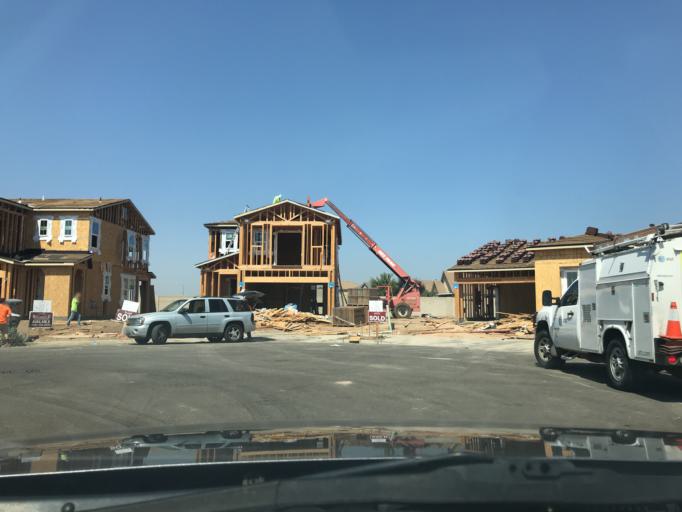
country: US
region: California
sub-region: Merced County
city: Merced
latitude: 37.3498
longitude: -120.4716
